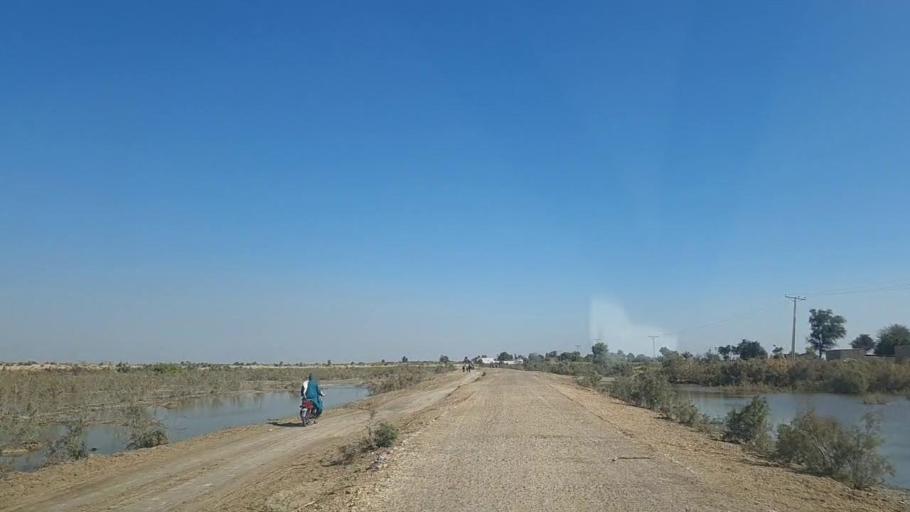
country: PK
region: Sindh
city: Sanghar
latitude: 26.2091
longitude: 68.8875
